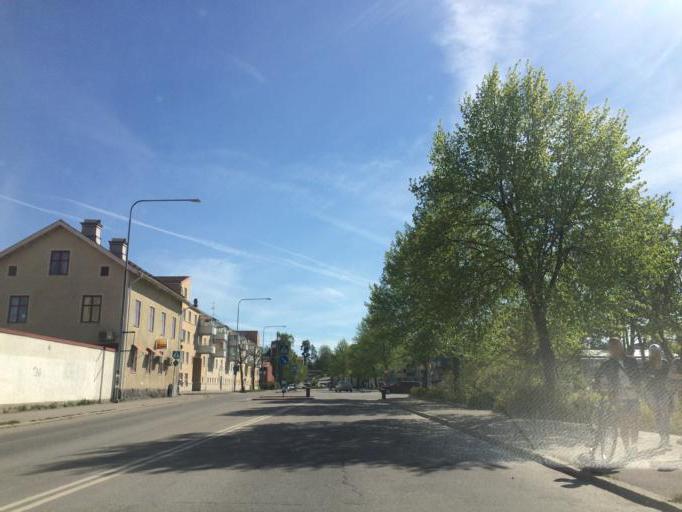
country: SE
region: Soedermanland
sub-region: Katrineholms Kommun
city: Katrineholm
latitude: 58.9953
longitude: 16.2018
